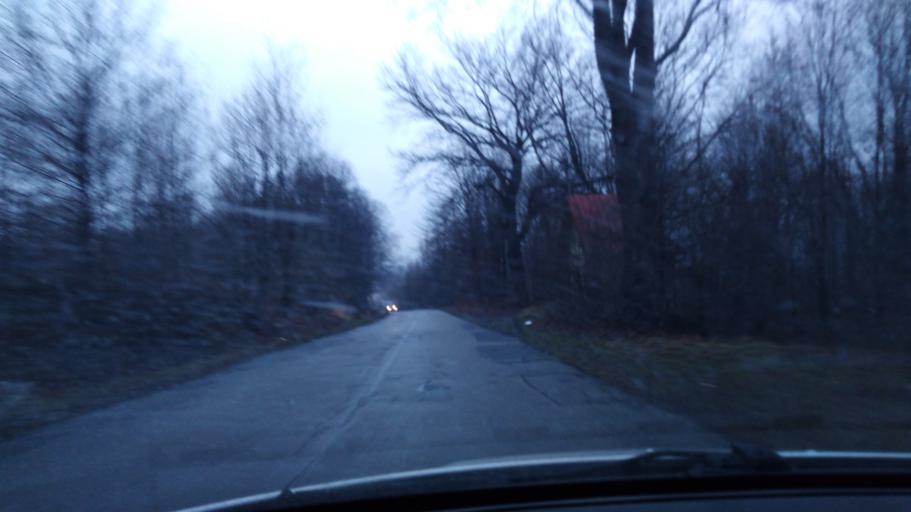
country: PL
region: Silesian Voivodeship
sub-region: Powiat zywiecki
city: Radziechowy
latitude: 49.6333
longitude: 19.1533
